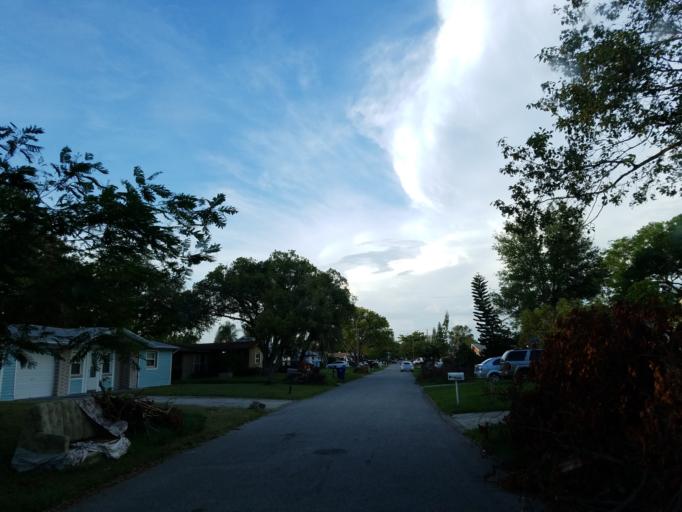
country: US
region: Florida
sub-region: Pasco County
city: Beacon Square
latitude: 28.2078
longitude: -82.7540
